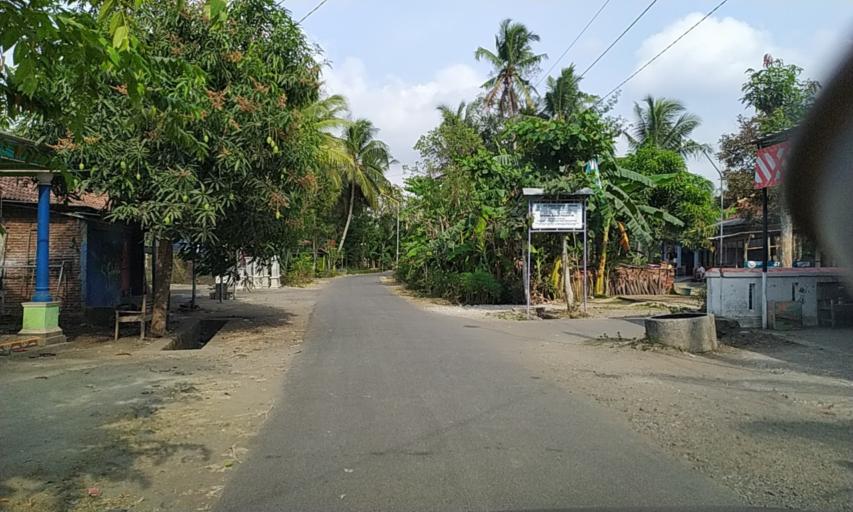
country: ID
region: Central Java
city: Kedungwringin
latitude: -7.4741
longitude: 108.7723
